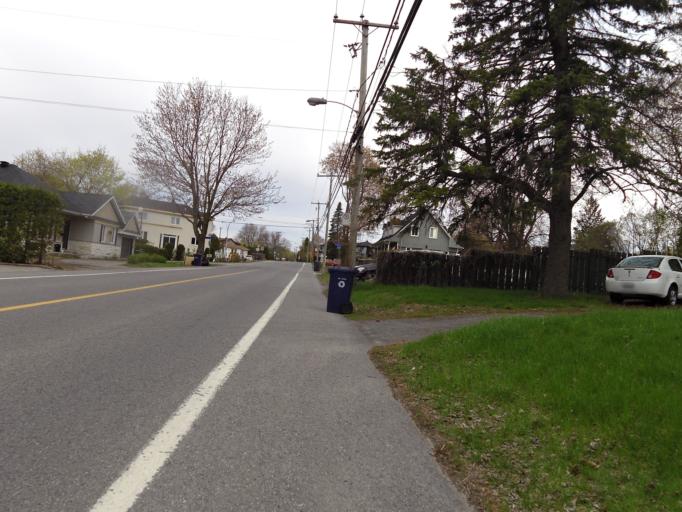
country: CA
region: Quebec
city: Dollard-Des Ormeaux
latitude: 45.5207
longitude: -73.8181
